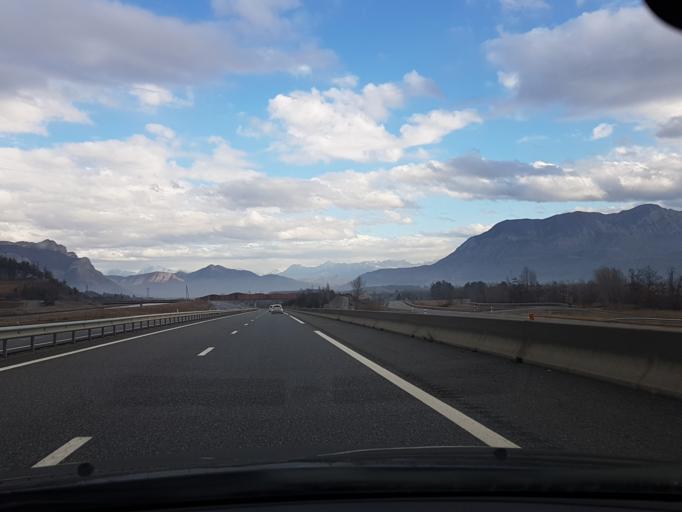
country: FR
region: Provence-Alpes-Cote d'Azur
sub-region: Departement des Hautes-Alpes
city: Laragne-Monteglin
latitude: 44.3410
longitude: 5.9031
